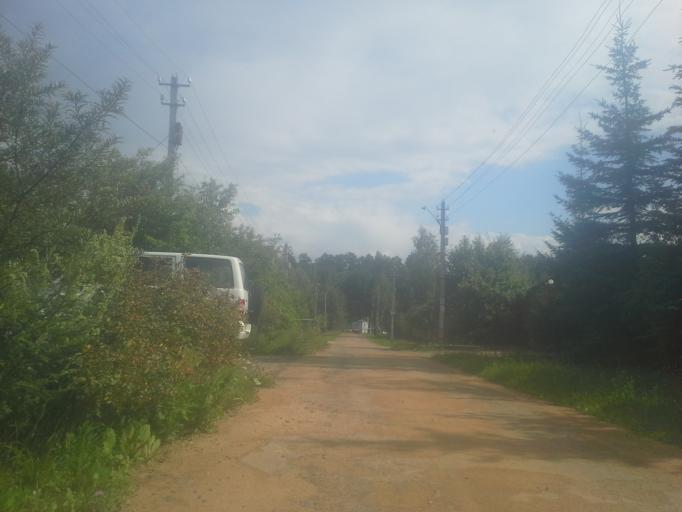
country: RU
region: Moskovskaya
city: Zhavoronki
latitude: 55.6425
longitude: 37.1437
